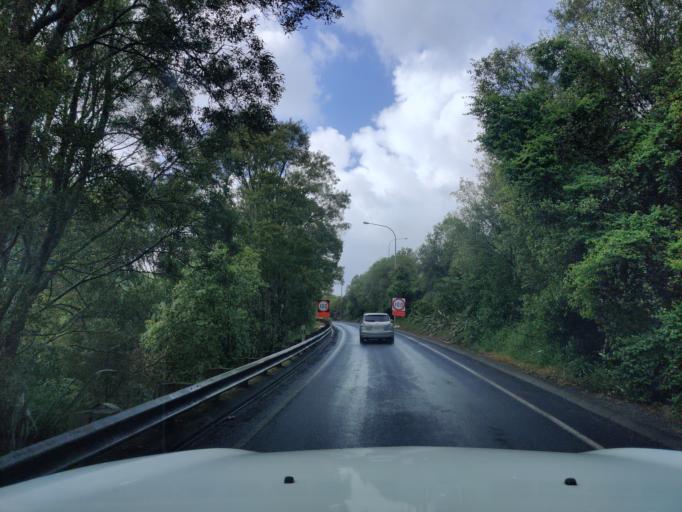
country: NZ
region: Waikato
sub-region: Hamilton City
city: Hamilton
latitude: -37.8284
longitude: 175.3582
